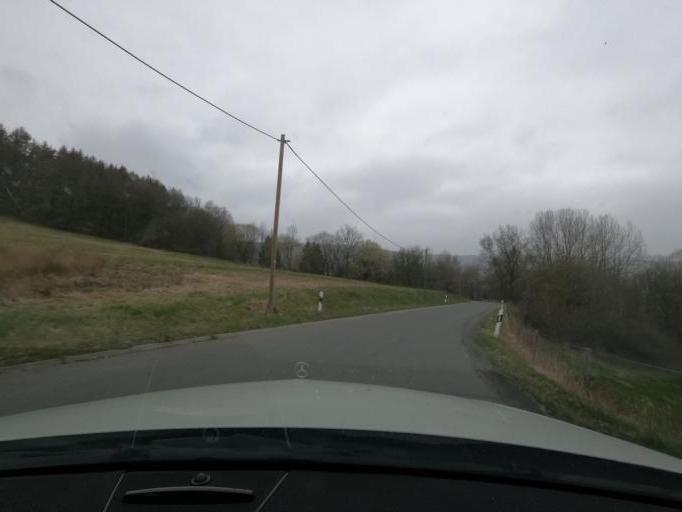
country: DE
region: Thuringia
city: Kella
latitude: 51.2234
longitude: 10.0827
